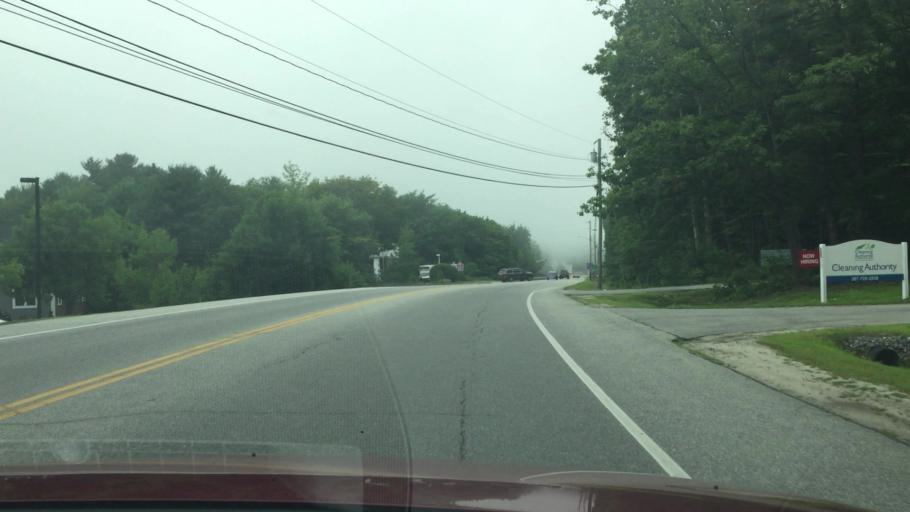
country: US
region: Maine
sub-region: Cumberland County
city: Freeport
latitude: 43.8618
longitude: -70.1046
